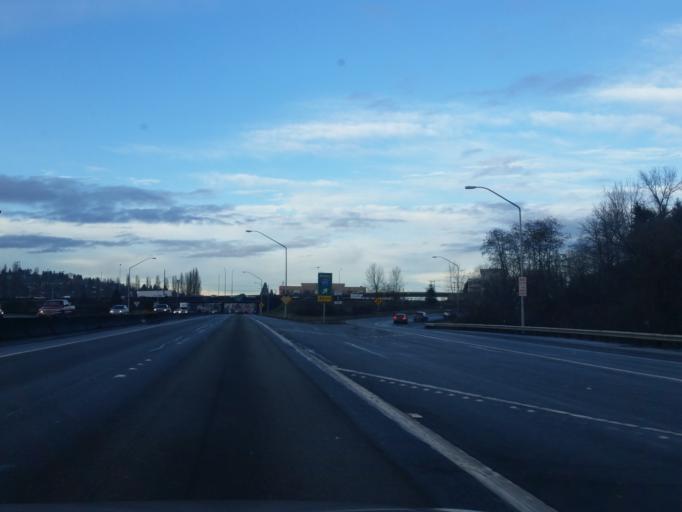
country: US
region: Washington
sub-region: King County
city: Renton
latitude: 47.4647
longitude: -122.2179
